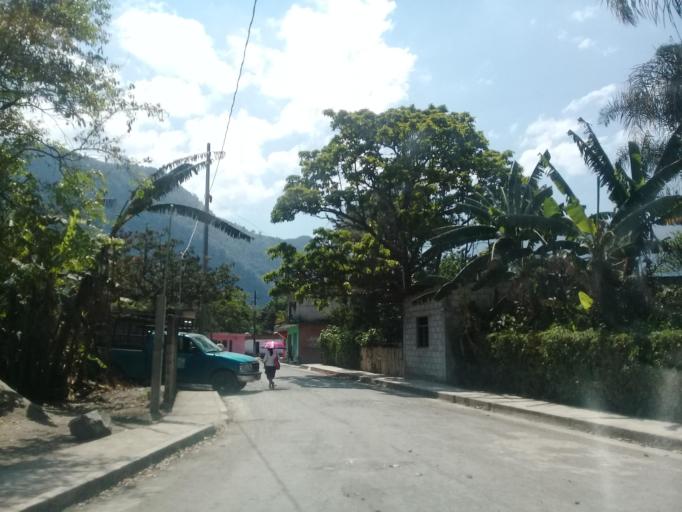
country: MX
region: Veracruz
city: Jalapilla
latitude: 18.8101
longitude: -97.0704
